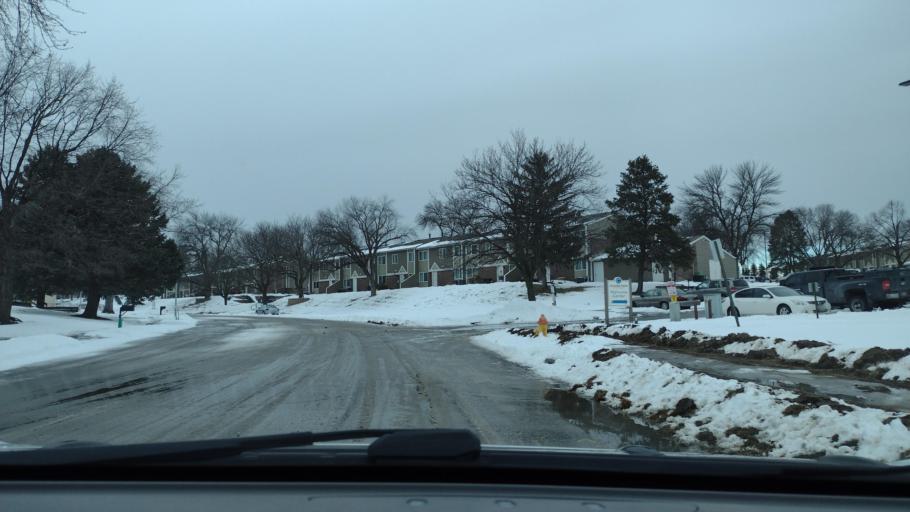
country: US
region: Nebraska
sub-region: Sarpy County
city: Bellevue
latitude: 41.1794
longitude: -95.9331
